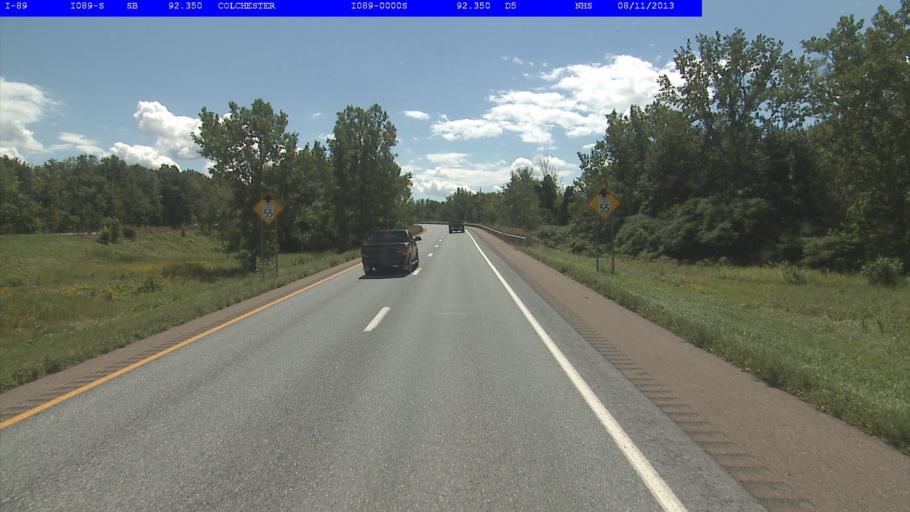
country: US
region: Vermont
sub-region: Chittenden County
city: Winooski
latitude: 44.5148
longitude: -73.1922
